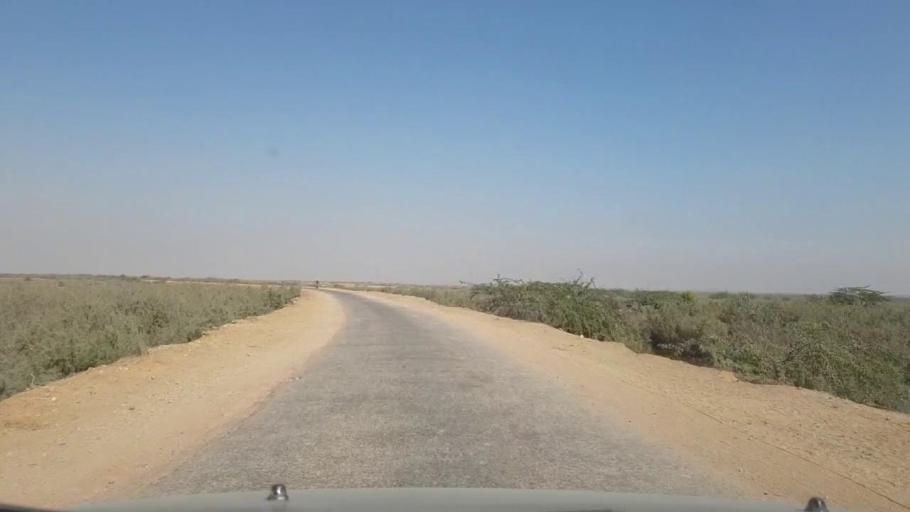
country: PK
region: Sindh
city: Thatta
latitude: 24.8238
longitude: 67.8930
